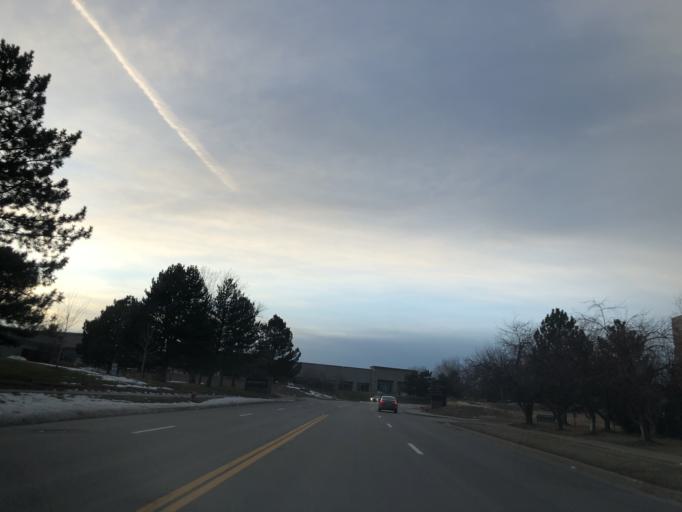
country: US
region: Colorado
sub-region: Douglas County
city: Meridian
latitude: 39.5597
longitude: -104.8634
